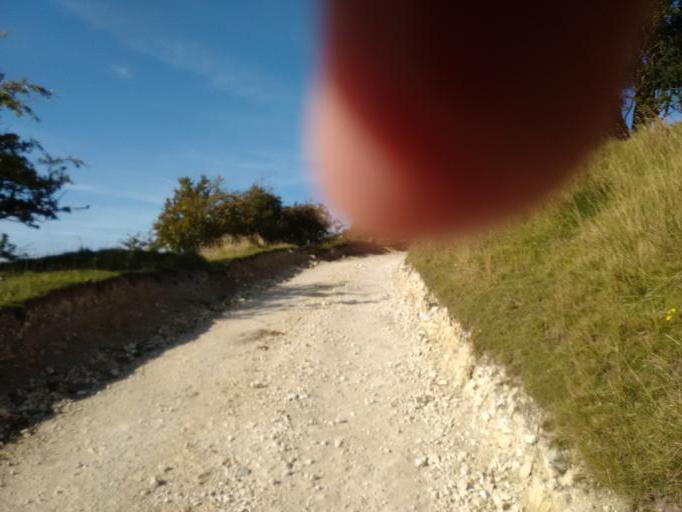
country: GB
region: England
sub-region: North Yorkshire
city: Thixendale
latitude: 54.0408
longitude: -0.7215
